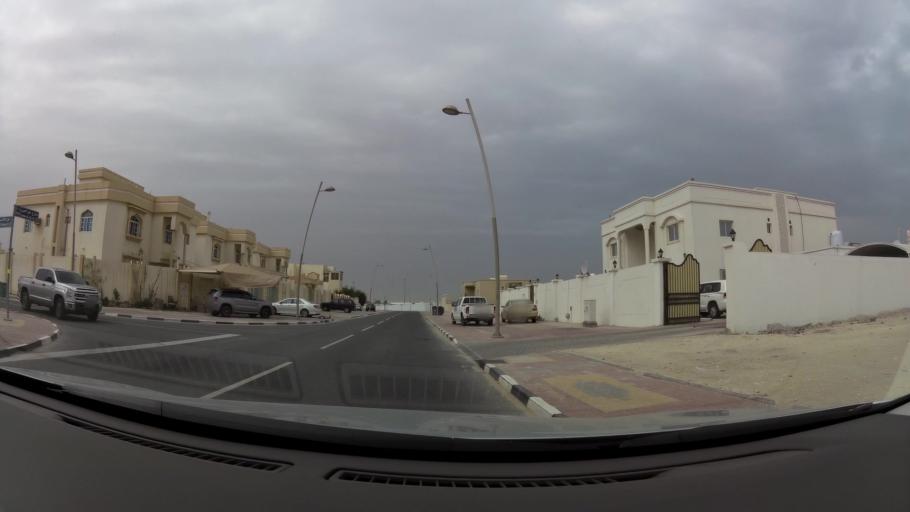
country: QA
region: Baladiyat ad Dawhah
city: Doha
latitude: 25.3452
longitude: 51.4855
